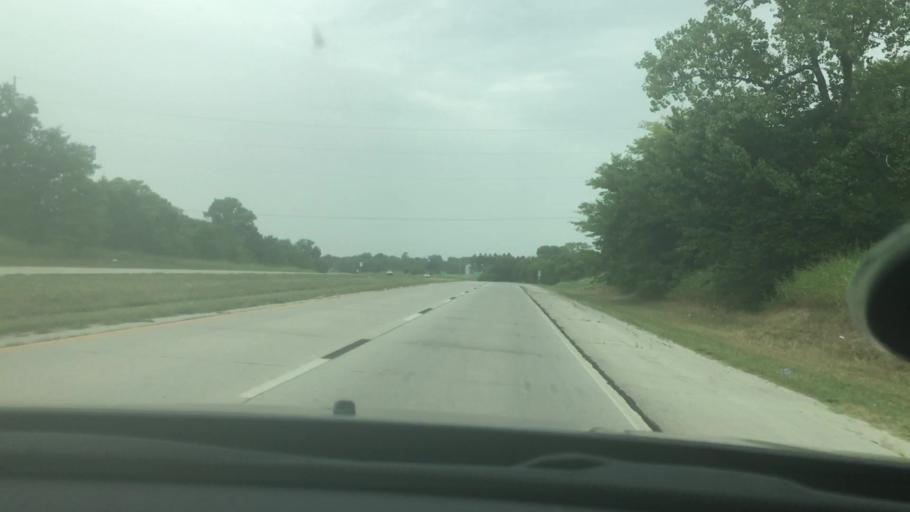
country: US
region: Oklahoma
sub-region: Pontotoc County
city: Ada
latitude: 34.7508
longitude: -96.6593
